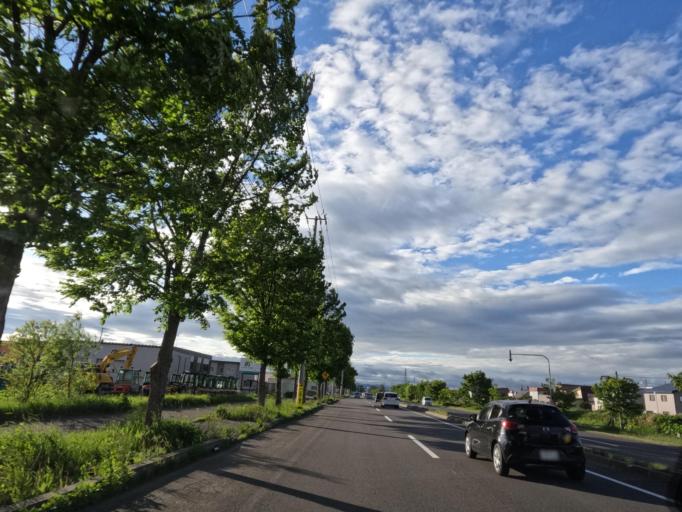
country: JP
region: Hokkaido
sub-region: Asahikawa-shi
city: Asahikawa
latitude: 43.7367
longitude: 142.3620
